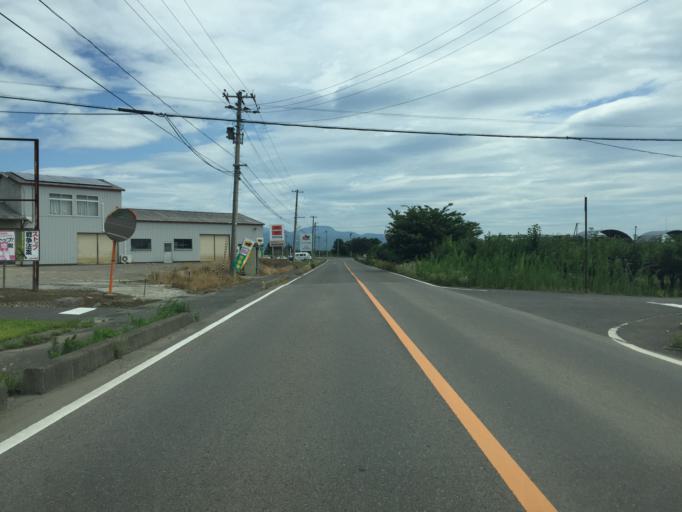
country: JP
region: Fukushima
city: Fukushima-shi
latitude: 37.7821
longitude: 140.3924
